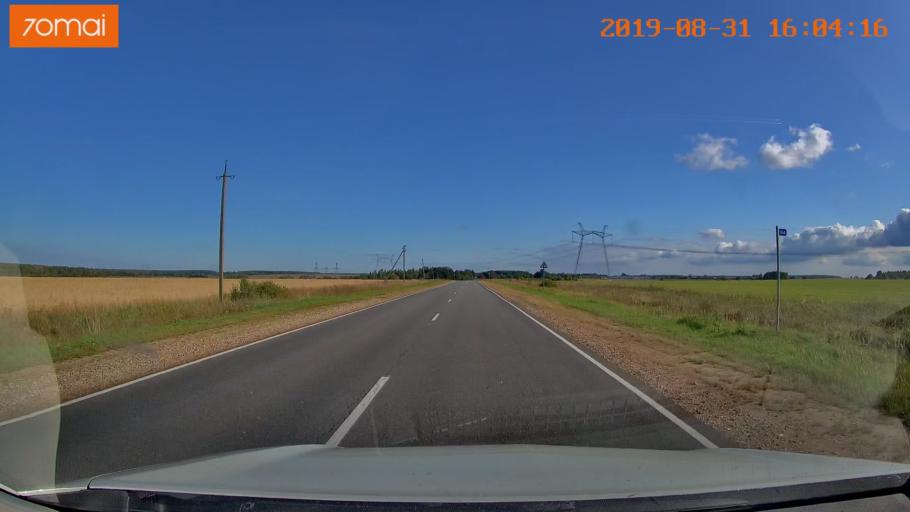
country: RU
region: Kaluga
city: Yukhnov
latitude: 54.6564
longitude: 35.3262
